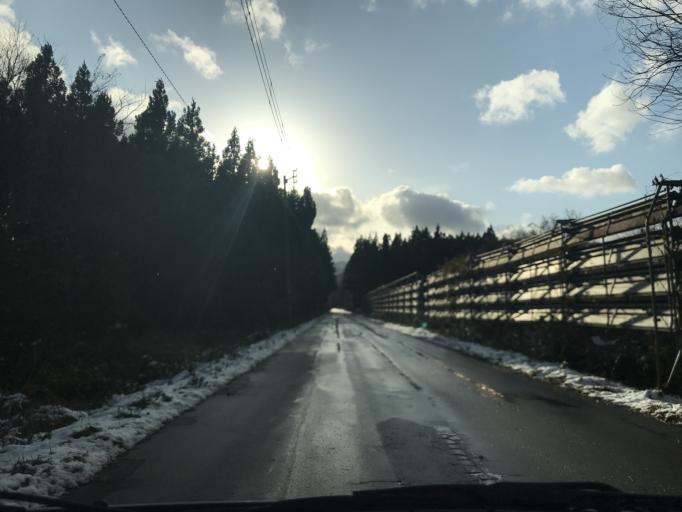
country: JP
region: Iwate
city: Kitakami
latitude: 39.2481
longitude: 141.0101
